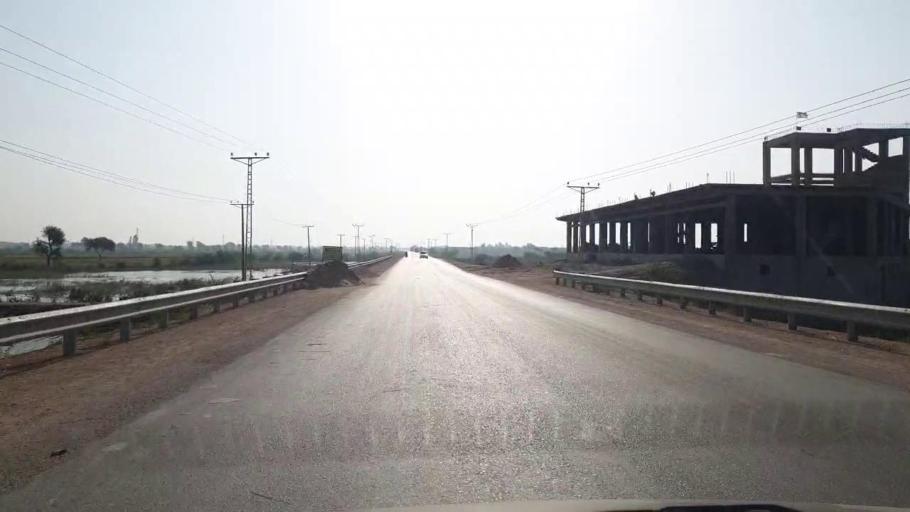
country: PK
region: Sindh
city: Badin
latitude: 24.6746
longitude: 68.8519
